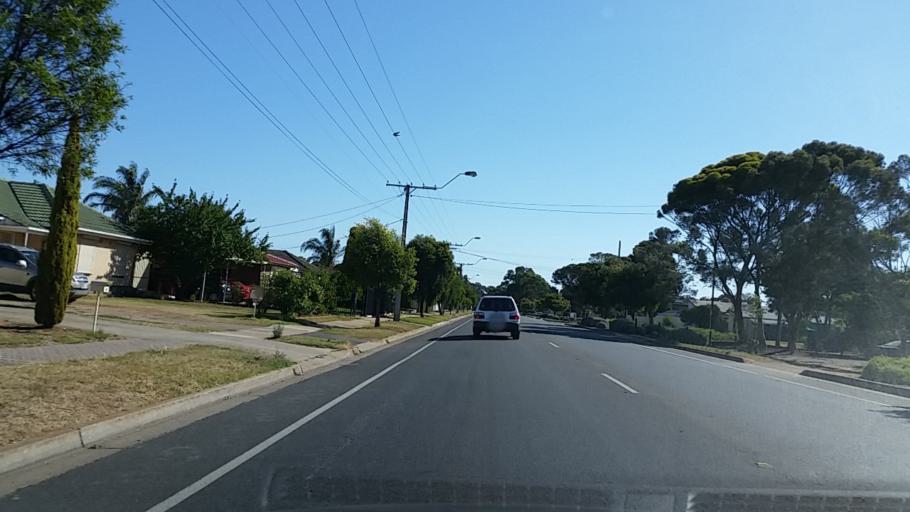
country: AU
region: South Australia
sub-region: Salisbury
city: Salisbury
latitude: -34.7739
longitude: 138.6470
